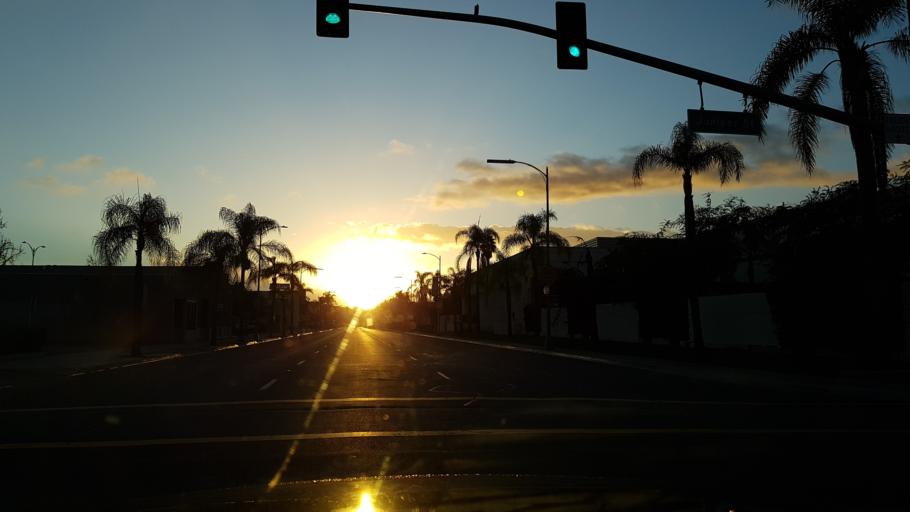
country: US
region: California
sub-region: San Diego County
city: Escondido
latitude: 33.1240
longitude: -117.0792
